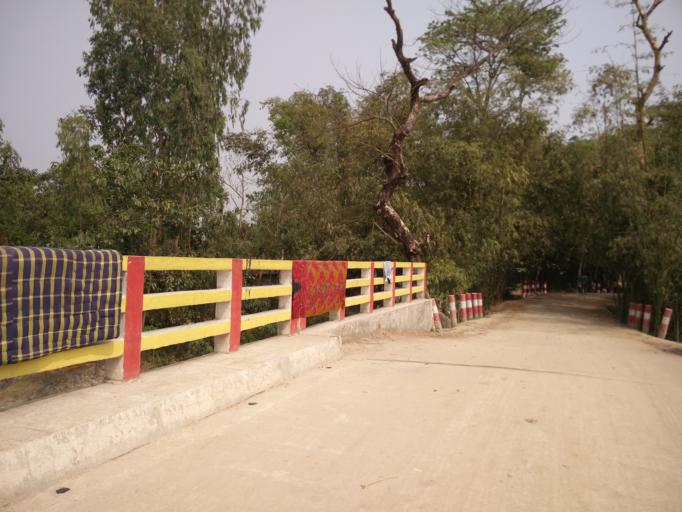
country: BD
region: Rangpur Division
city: Nageswari
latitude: 25.8907
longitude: 89.7187
